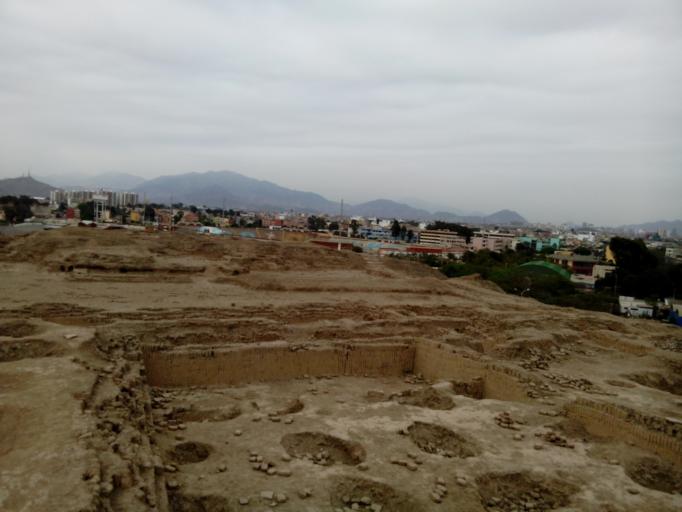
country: PE
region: Callao
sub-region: Callao
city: Callao
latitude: -12.0602
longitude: -77.0865
